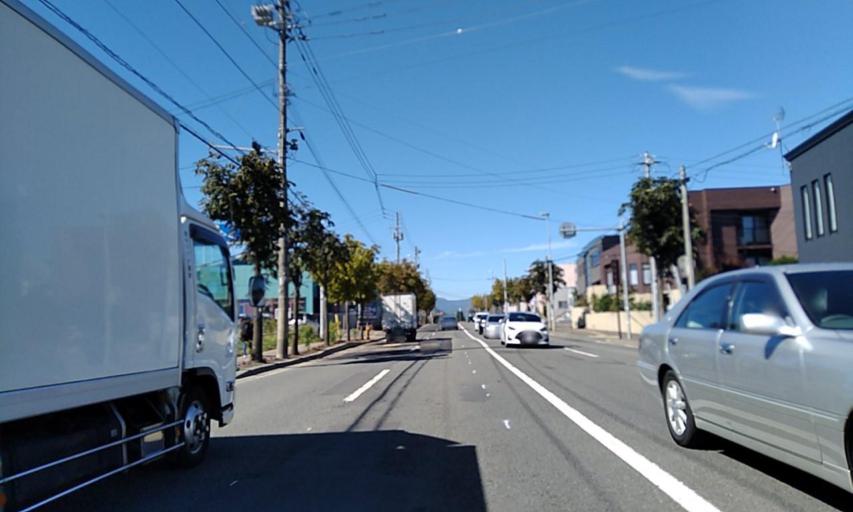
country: JP
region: Hokkaido
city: Sapporo
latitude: 43.0033
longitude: 141.3911
